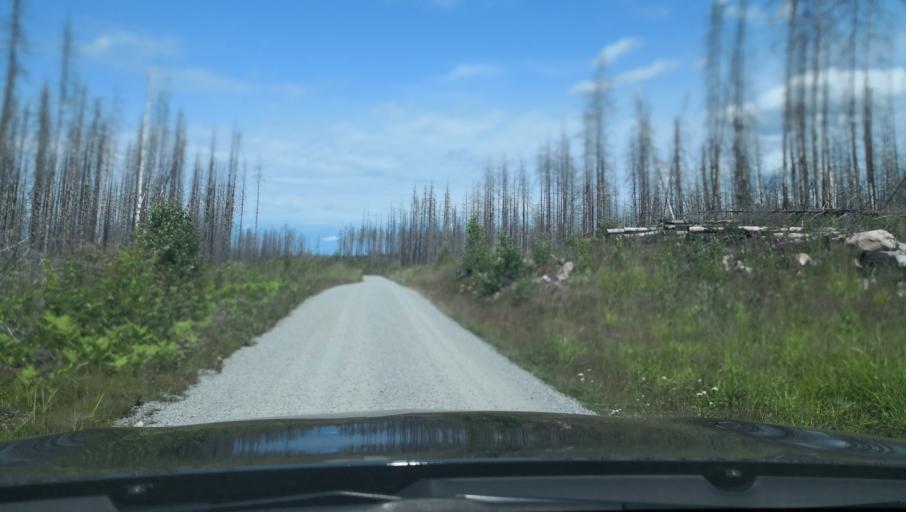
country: SE
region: Vaestmanland
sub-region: Surahammars Kommun
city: Ramnas
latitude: 59.9008
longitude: 16.1425
